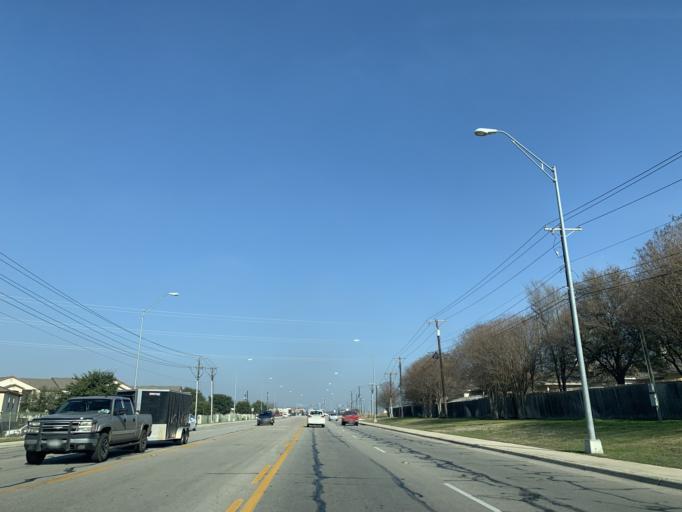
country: US
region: Texas
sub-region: Williamson County
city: Round Rock
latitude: 30.5399
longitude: -97.6511
